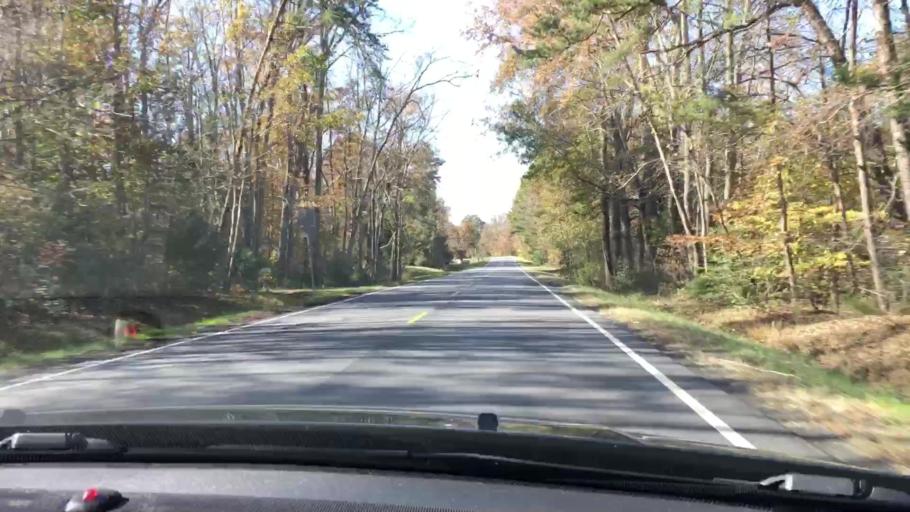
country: US
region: Virginia
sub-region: King William County
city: King William
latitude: 37.6740
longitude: -76.9801
